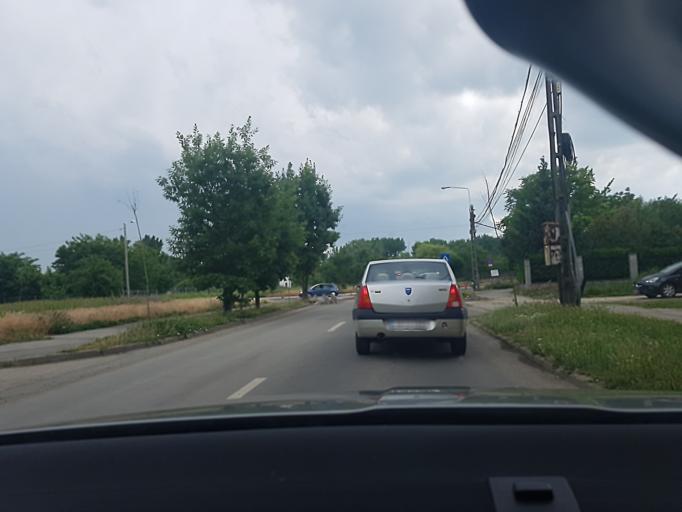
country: RO
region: Timis
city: Timisoara
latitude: 45.7360
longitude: 21.2439
